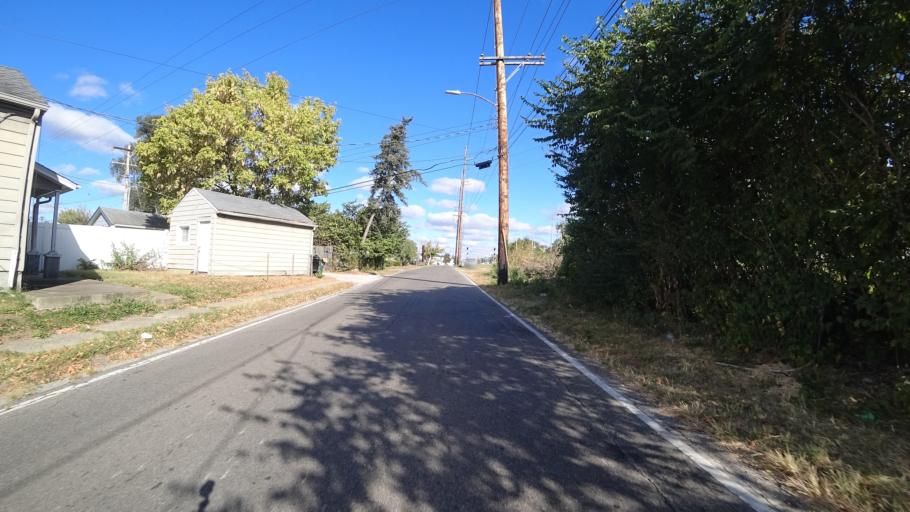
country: US
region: Ohio
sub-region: Butler County
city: Fairfield
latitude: 39.3669
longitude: -84.5492
